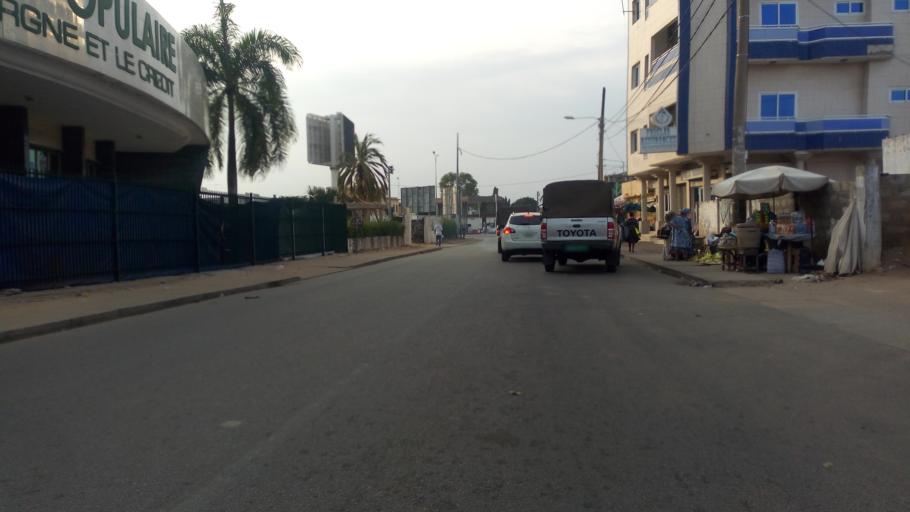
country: TG
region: Maritime
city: Lome
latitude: 6.1351
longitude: 1.2194
